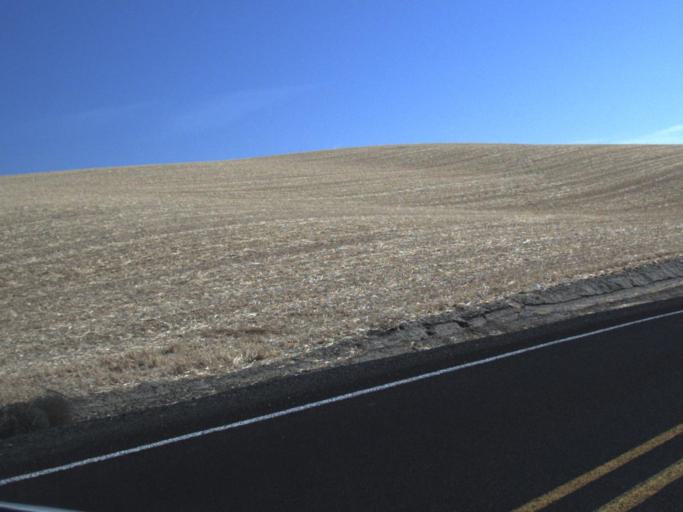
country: US
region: Washington
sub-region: Walla Walla County
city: Walla Walla
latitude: 46.1110
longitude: -118.3734
